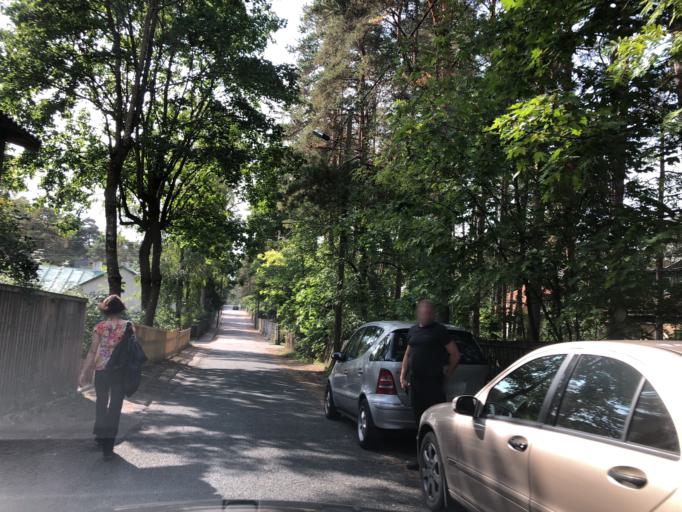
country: EE
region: Harju
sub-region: Tallinna linn
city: Tallinn
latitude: 59.3825
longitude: 24.6918
